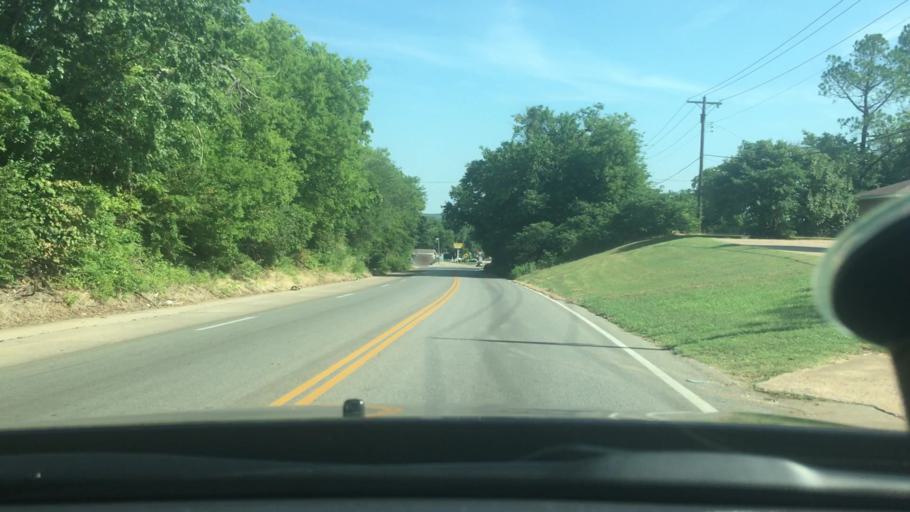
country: US
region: Oklahoma
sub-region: Garvin County
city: Pauls Valley
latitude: 34.7266
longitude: -97.2129
